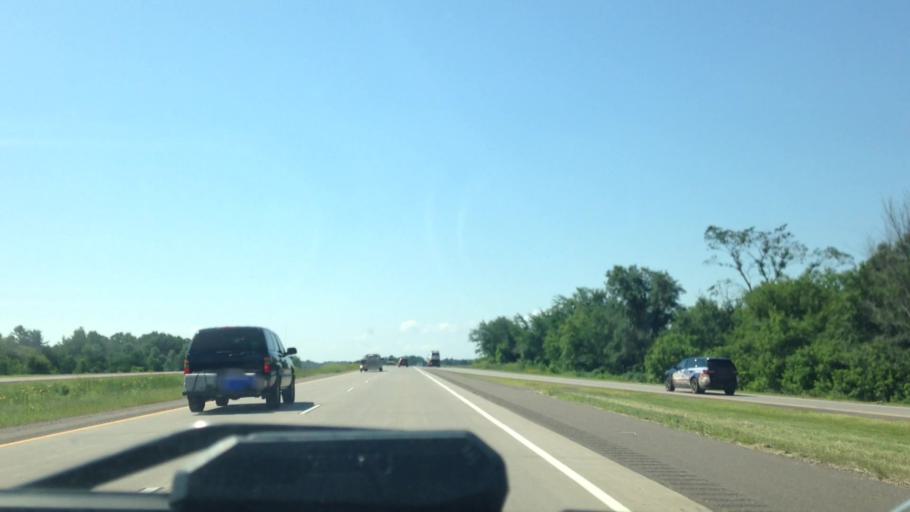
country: US
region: Wisconsin
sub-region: Barron County
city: Rice Lake
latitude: 45.4708
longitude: -91.7586
